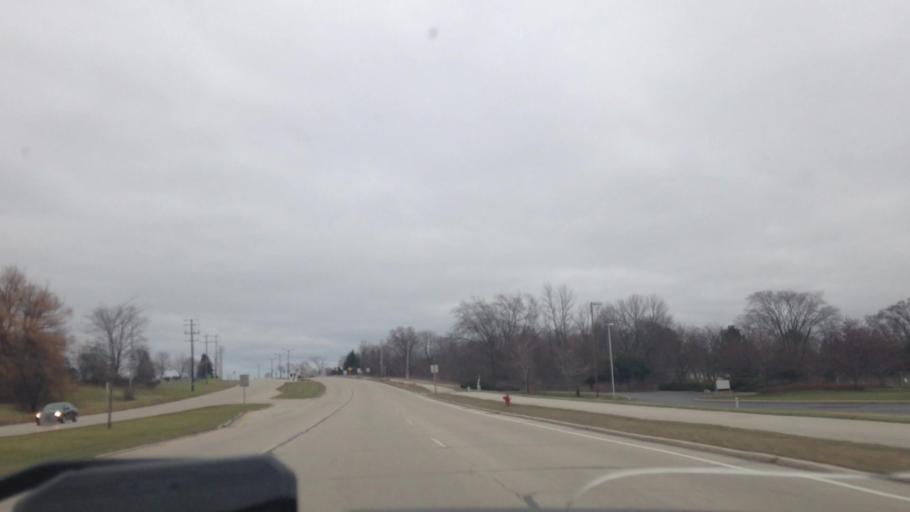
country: US
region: Wisconsin
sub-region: Waukesha County
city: Menomonee Falls
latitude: 43.1775
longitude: -88.0827
